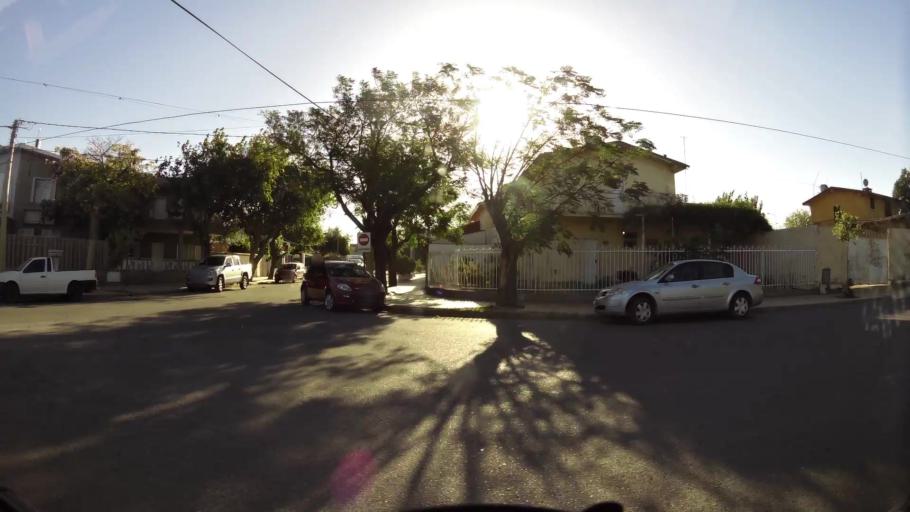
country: AR
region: San Juan
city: San Juan
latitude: -31.5491
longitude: -68.5195
